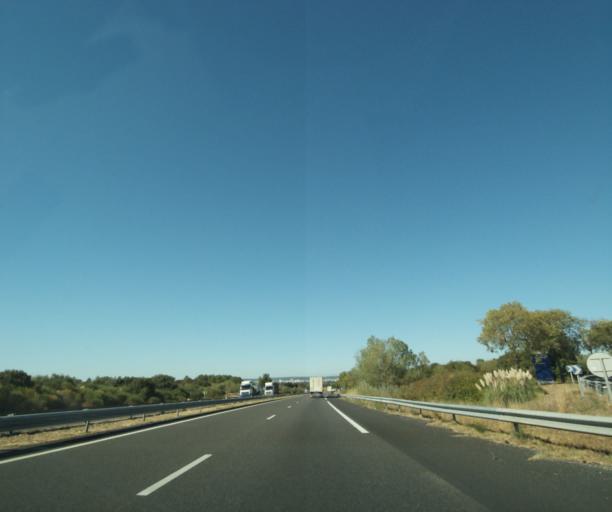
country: FR
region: Languedoc-Roussillon
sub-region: Departement du Gard
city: Caissargues
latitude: 43.7873
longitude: 4.4017
